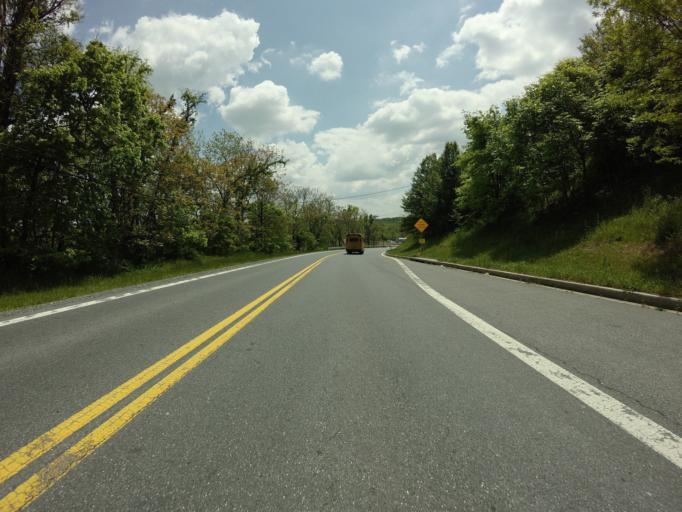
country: US
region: Maryland
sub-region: Frederick County
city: Green Valley
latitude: 39.2942
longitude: -77.3156
